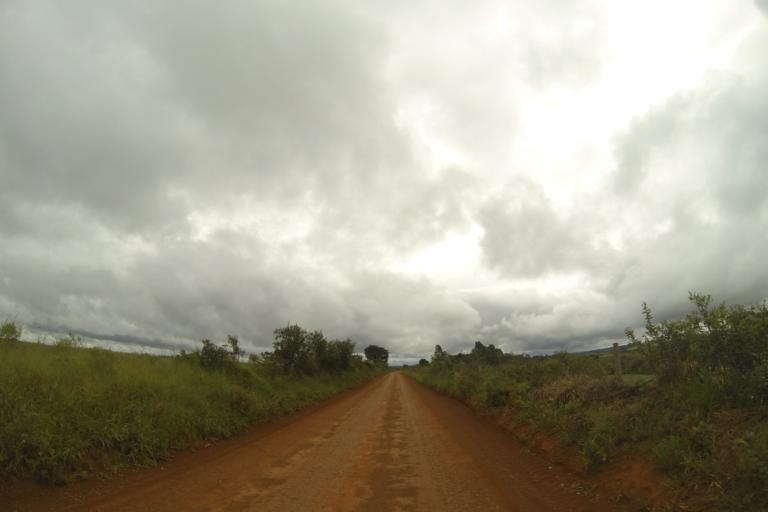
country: BR
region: Minas Gerais
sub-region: Campos Altos
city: Campos Altos
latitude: -19.8569
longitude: -46.3140
